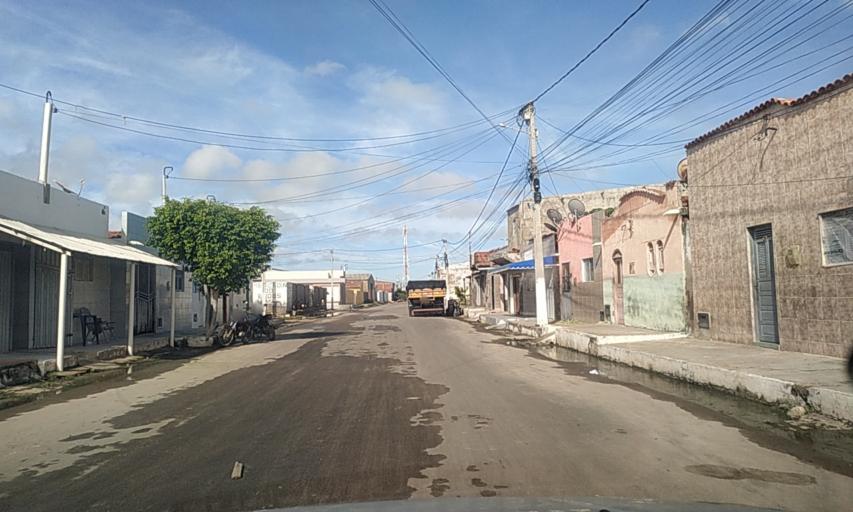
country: BR
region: Rio Grande do Norte
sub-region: Areia Branca
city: Areia Branca
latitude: -4.9492
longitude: -37.1224
